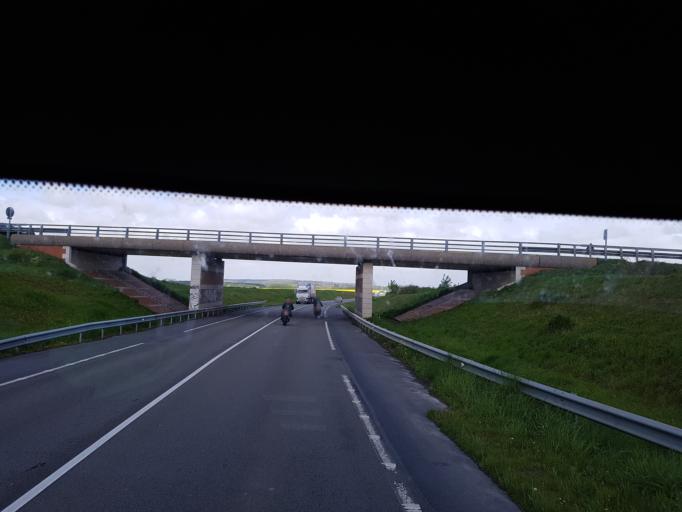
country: FR
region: Nord-Pas-de-Calais
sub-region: Departement du Nord
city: Rumilly-en-Cambresis
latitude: 50.1427
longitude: 3.2120
